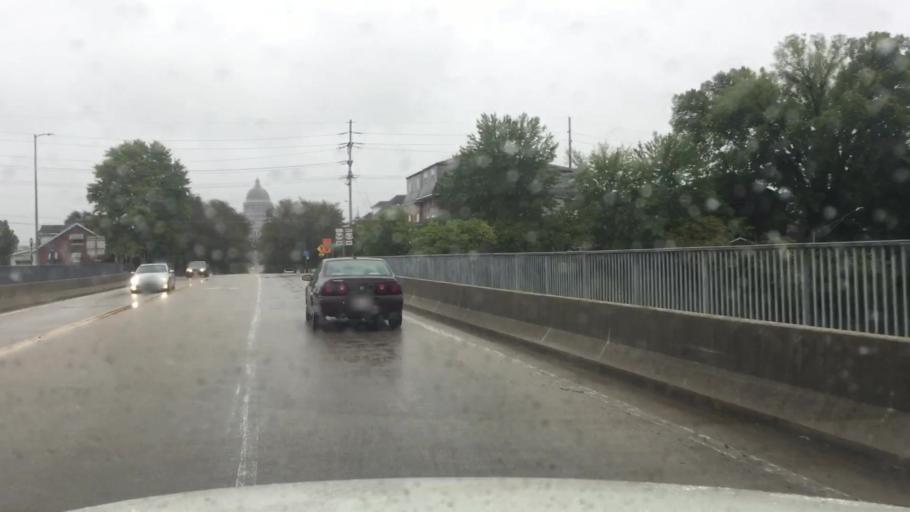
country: US
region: Missouri
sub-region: Cole County
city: Jefferson City
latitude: 38.5851
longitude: -92.1815
